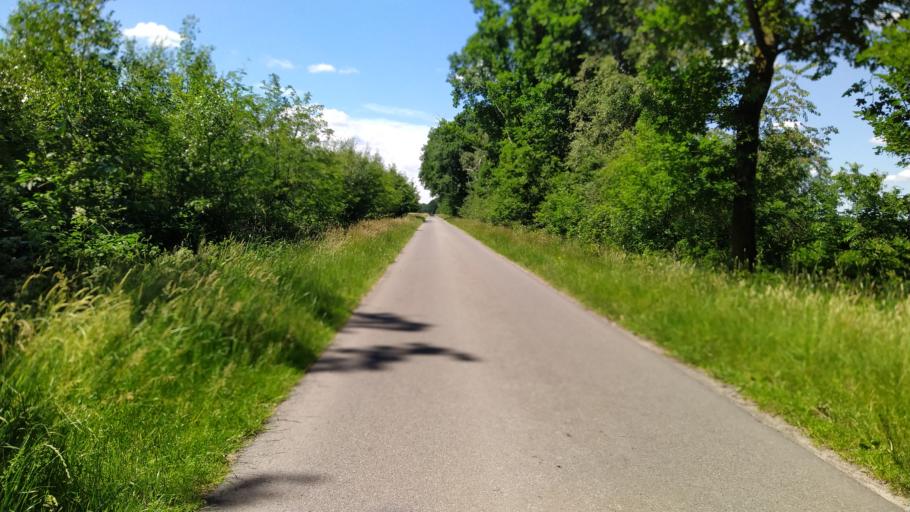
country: DE
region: Lower Saxony
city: Oldendorf
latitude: 53.5597
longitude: 9.2282
